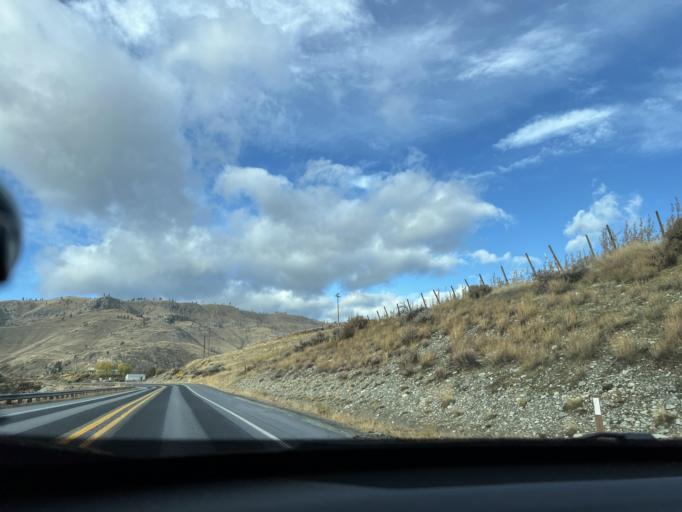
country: US
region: Washington
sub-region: Chelan County
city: Chelan
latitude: 47.8626
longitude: -119.9348
